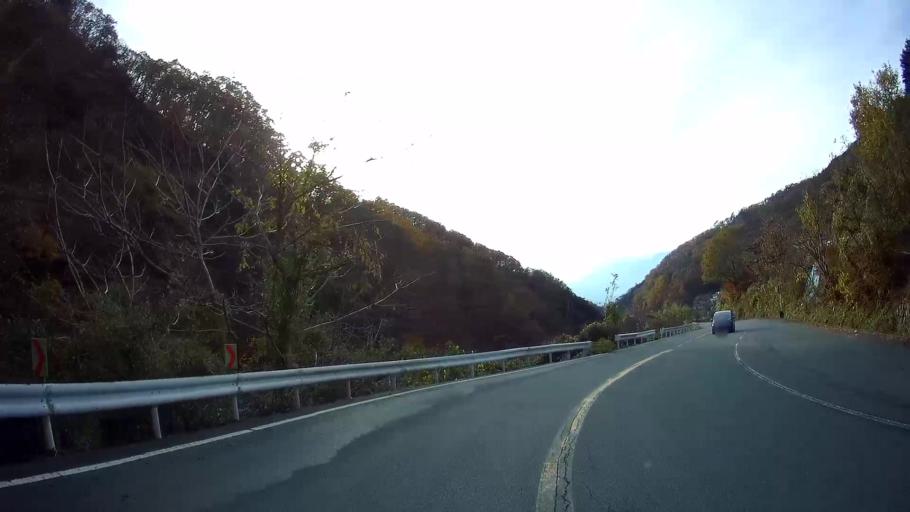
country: JP
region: Yamanashi
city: Fujikawaguchiko
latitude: 35.4754
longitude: 138.5553
